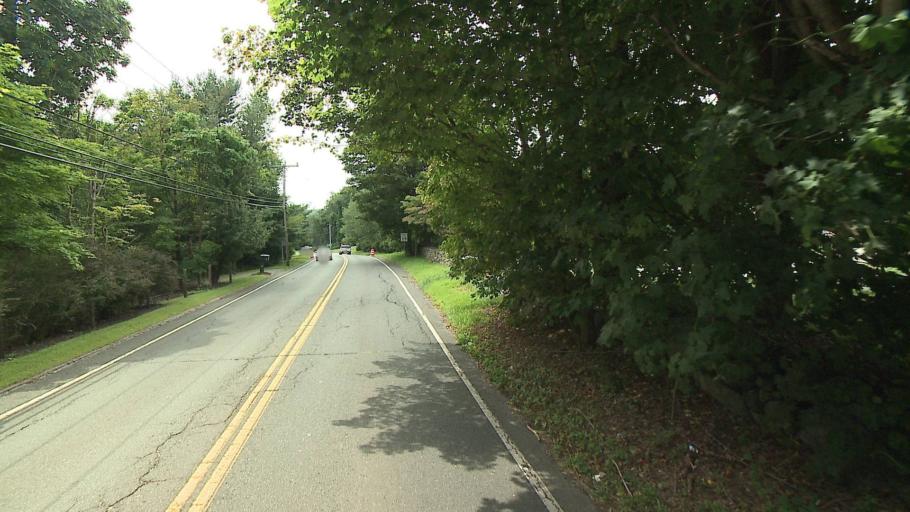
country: US
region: New York
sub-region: Putnam County
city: Putnam Lake
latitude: 41.4490
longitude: -73.5247
